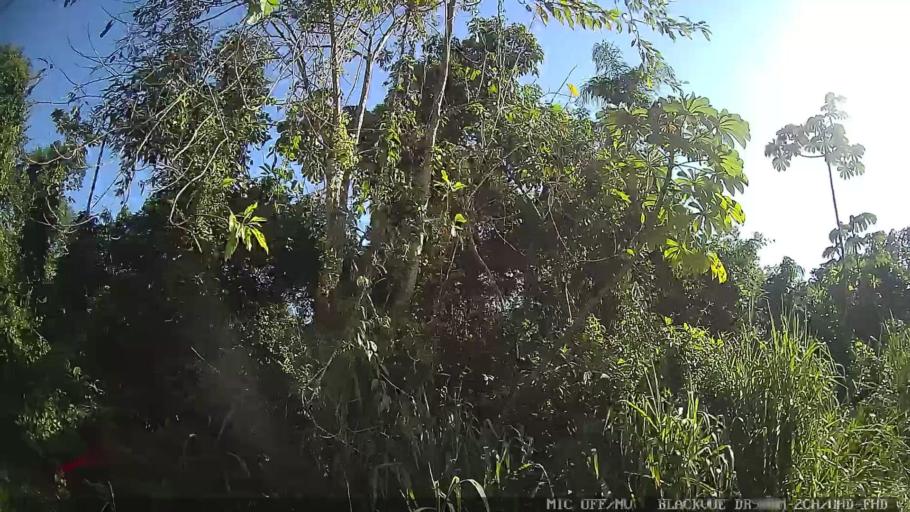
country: BR
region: Sao Paulo
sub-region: Santos
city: Santos
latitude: -23.9005
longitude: -46.3037
